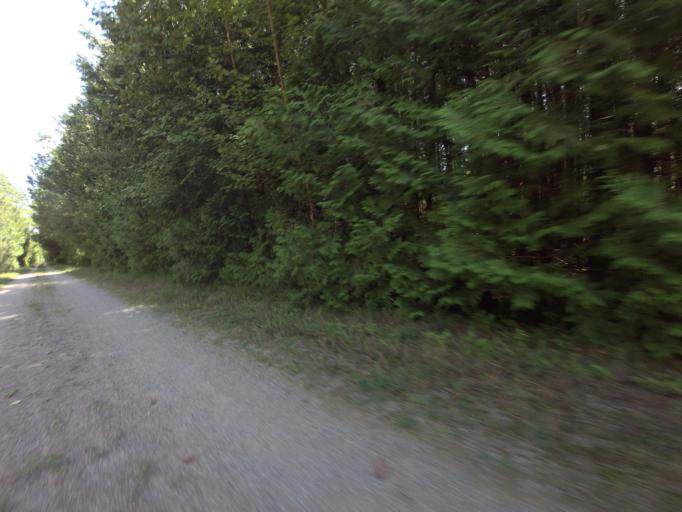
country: CA
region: Ontario
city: Orangeville
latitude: 43.7743
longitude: -80.1832
